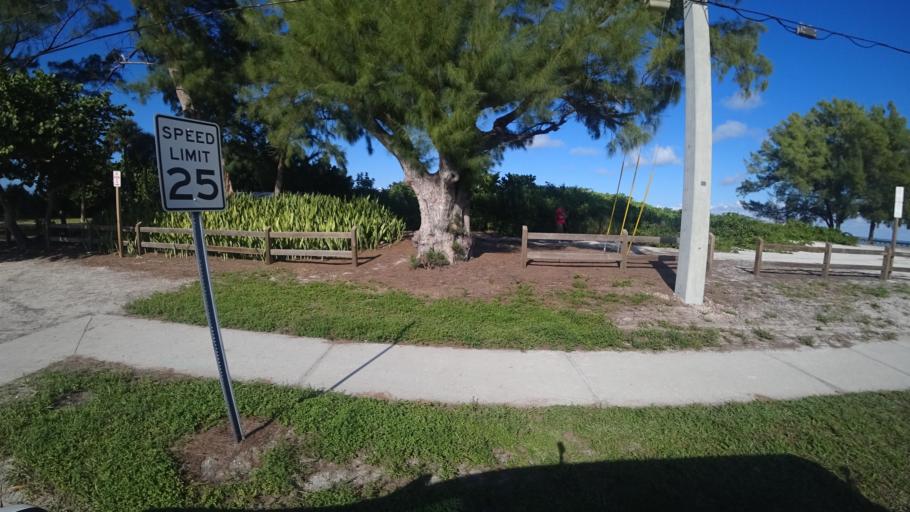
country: US
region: Florida
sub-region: Manatee County
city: Anna Maria
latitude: 27.5335
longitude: -82.7336
